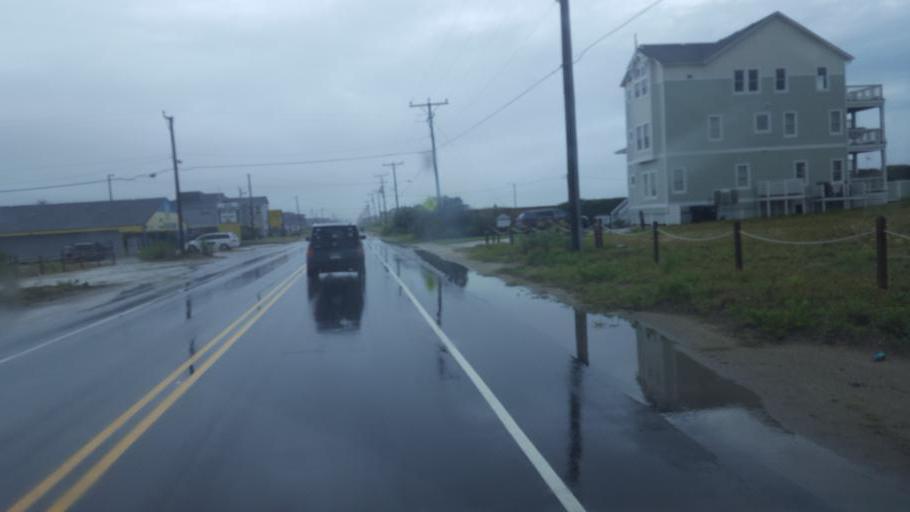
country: US
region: North Carolina
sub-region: Dare County
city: Kill Devil Hills
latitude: 36.0428
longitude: -75.6746
